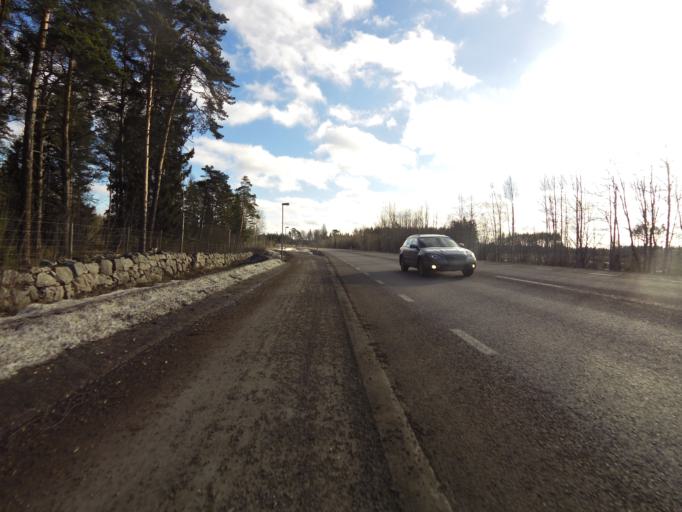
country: SE
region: Gaevleborg
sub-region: Gavle Kommun
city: Gavle
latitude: 60.6460
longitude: 17.2591
